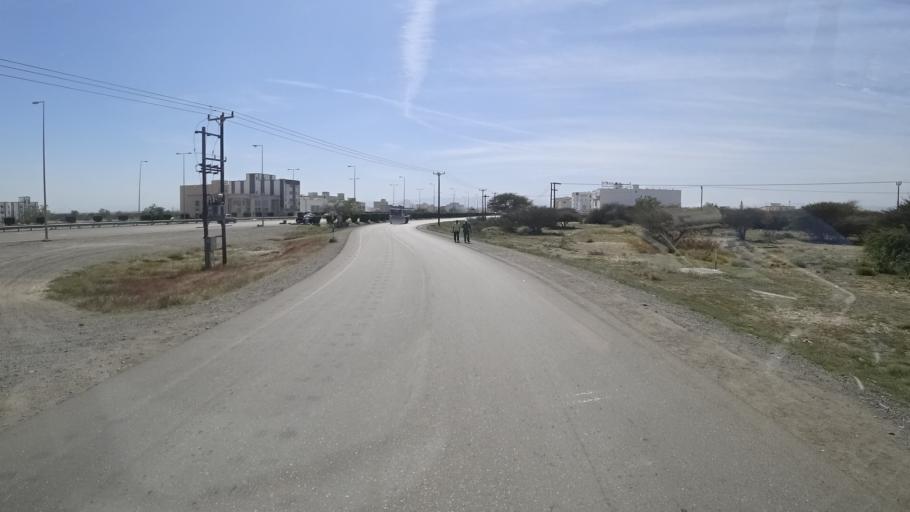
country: OM
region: Al Batinah
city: Al Liwa'
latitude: 24.4210
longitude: 56.6069
